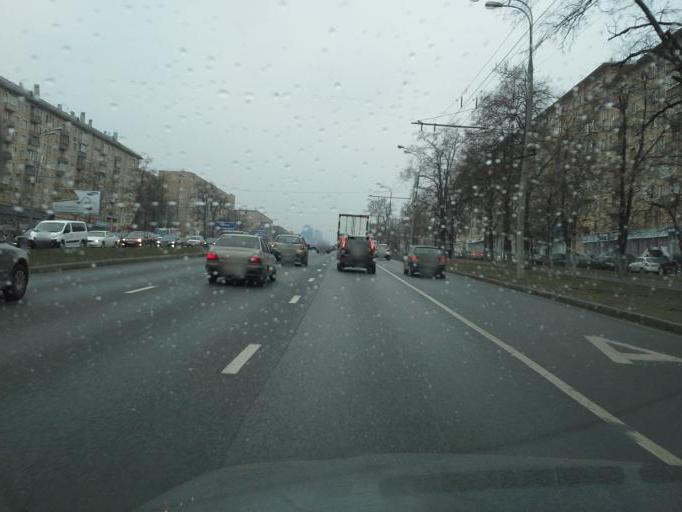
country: RU
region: Moskovskaya
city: Semenovskoye
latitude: 55.6821
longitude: 37.5364
